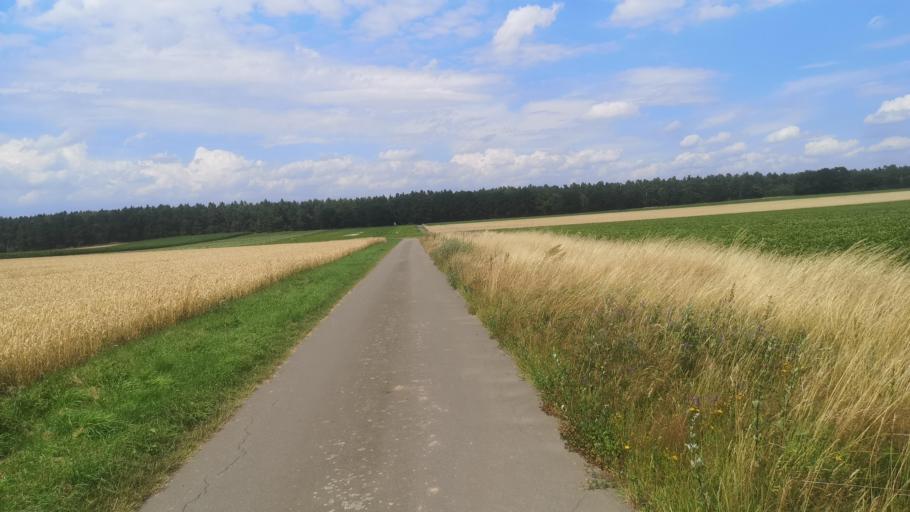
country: DE
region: Lower Saxony
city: Dahlem
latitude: 53.2305
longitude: 10.7461
